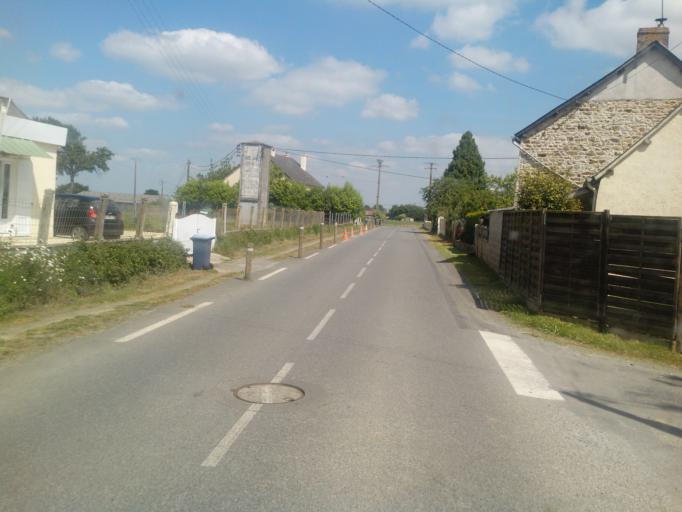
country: FR
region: Brittany
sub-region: Departement d'Ille-et-Vilaine
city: Saint-Medard-sur-Ille
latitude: 48.2679
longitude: -1.6530
